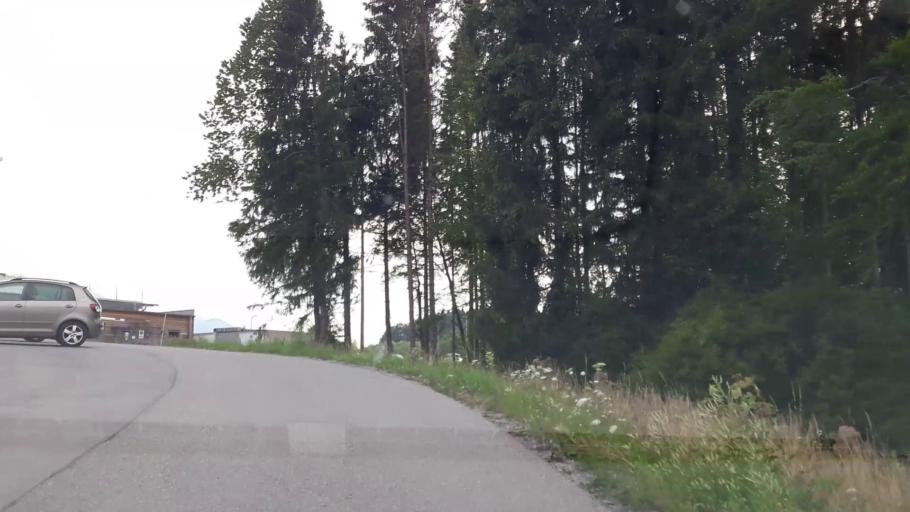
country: DE
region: Bavaria
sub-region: Upper Bavaria
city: Bergen
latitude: 47.8296
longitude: 12.5916
